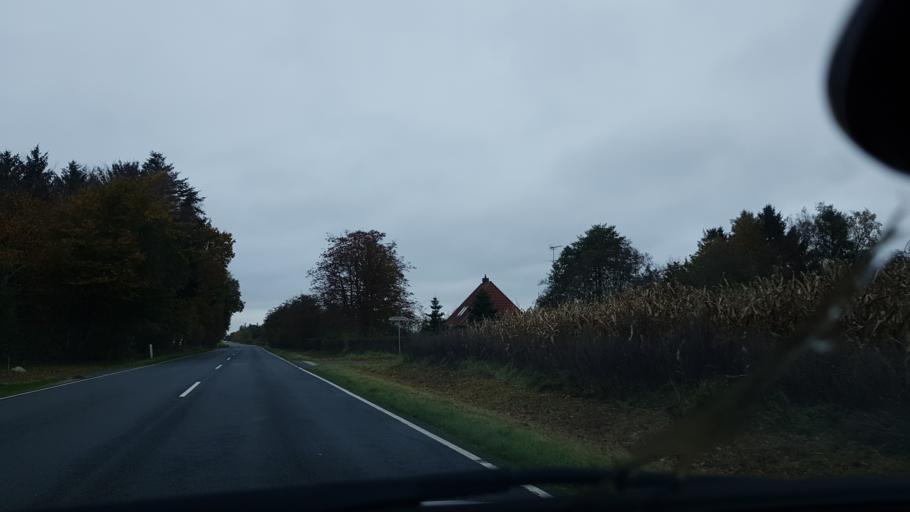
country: DK
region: South Denmark
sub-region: Esbjerg Kommune
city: Ribe
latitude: 55.2985
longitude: 8.8113
